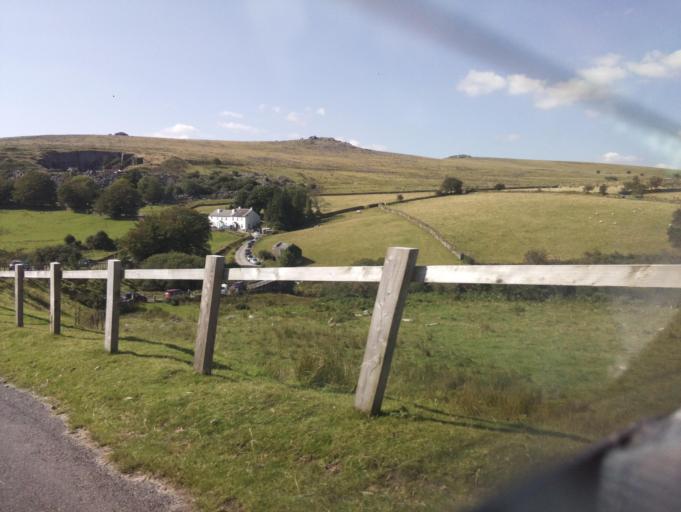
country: GB
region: England
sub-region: Devon
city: Horrabridge
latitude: 50.5569
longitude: -4.0471
